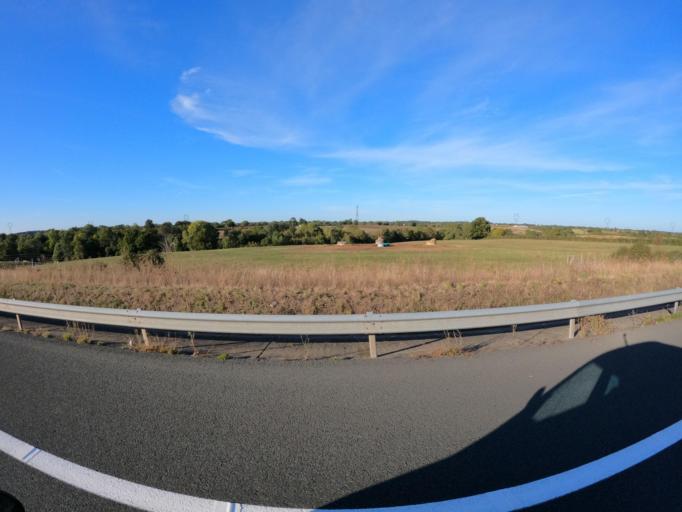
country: FR
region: Pays de la Loire
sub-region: Departement de Maine-et-Loire
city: Chemille-Melay
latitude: 47.2476
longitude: -0.6951
